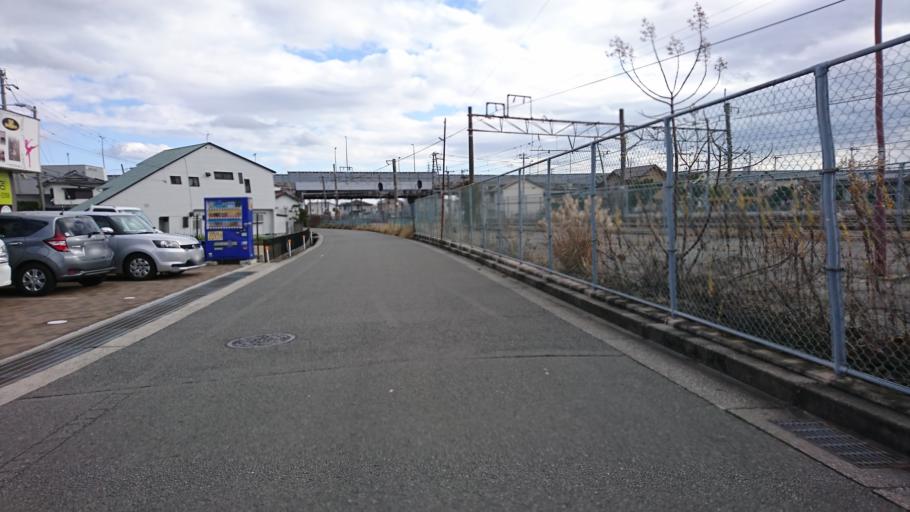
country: JP
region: Hyogo
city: Kakogawacho-honmachi
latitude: 34.7839
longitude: 134.8155
